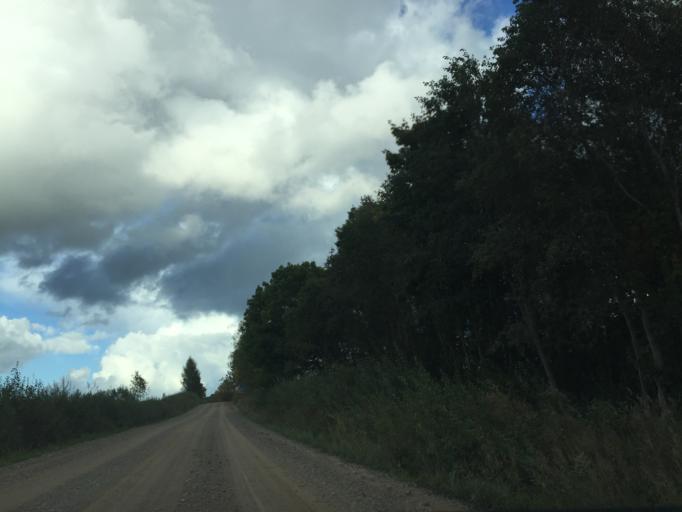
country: LV
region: Amatas Novads
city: Drabesi
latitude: 57.0619
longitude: 25.1746
